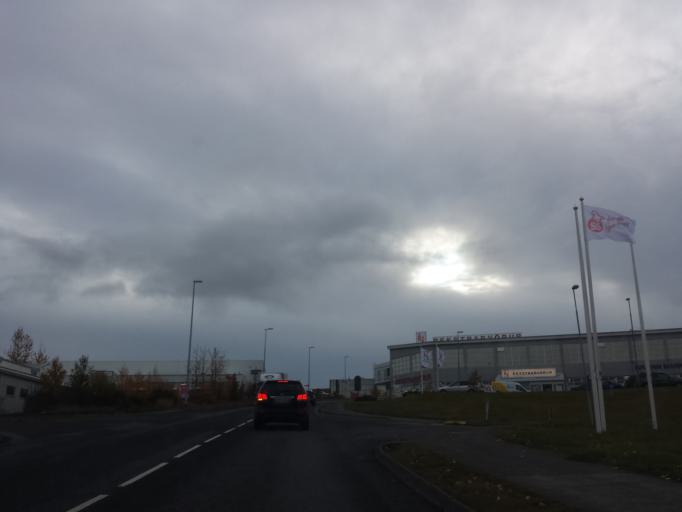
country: IS
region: Capital Region
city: Reykjavik
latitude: 64.1218
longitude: -21.7969
